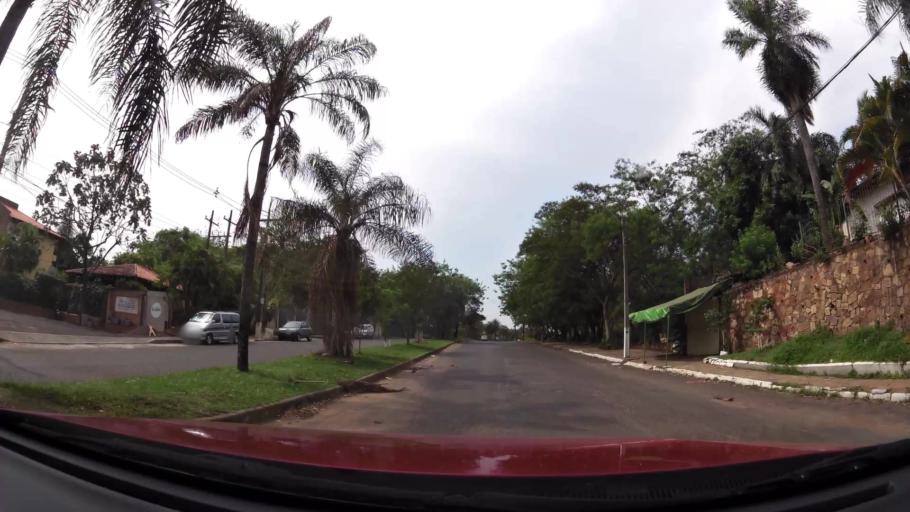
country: PY
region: Asuncion
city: Asuncion
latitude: -25.2798
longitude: -57.5792
